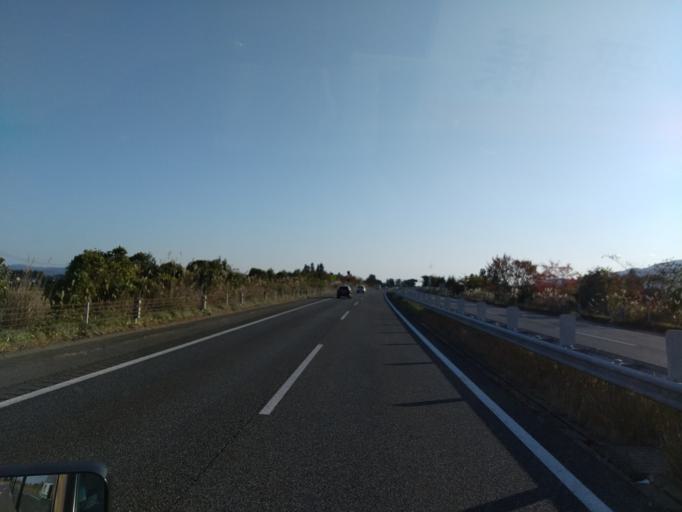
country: JP
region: Iwate
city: Morioka-shi
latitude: 39.5748
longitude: 141.1208
